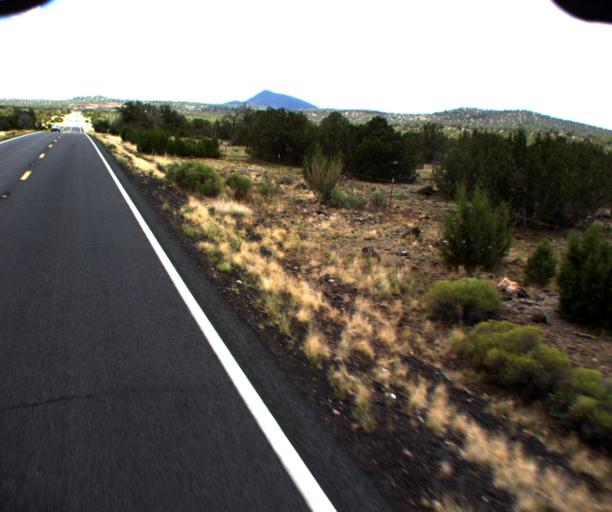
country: US
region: Arizona
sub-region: Coconino County
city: Parks
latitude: 35.5714
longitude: -111.9251
